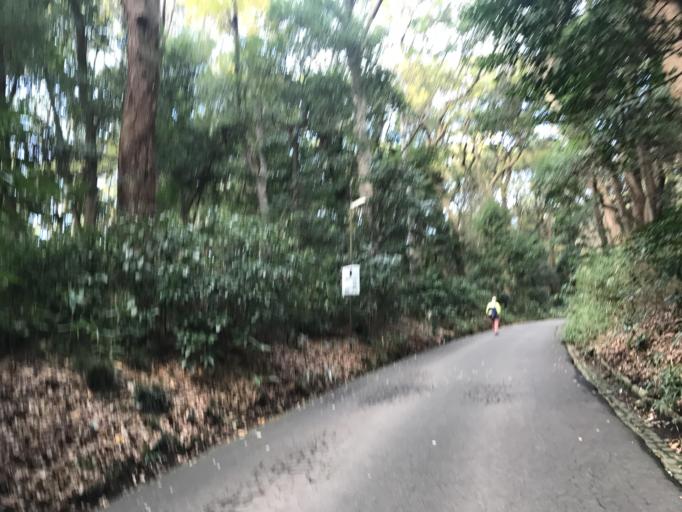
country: JP
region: Tokyo
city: Tokyo
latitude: 35.6725
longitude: 139.6979
